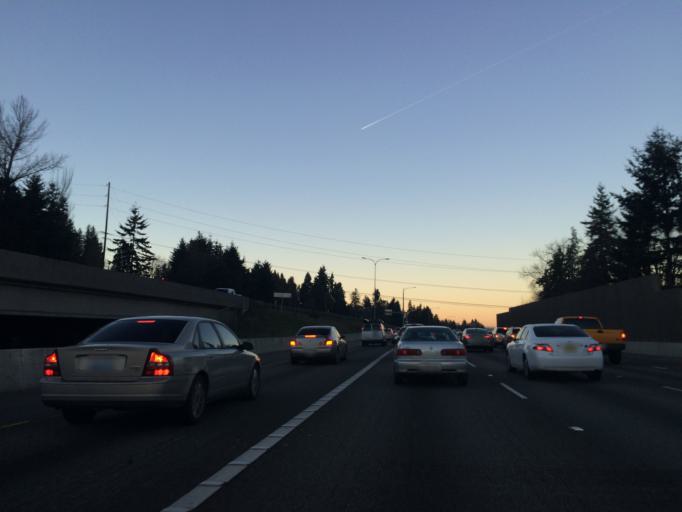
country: US
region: Washington
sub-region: Snohomish County
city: Everett
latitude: 47.9478
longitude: -122.1984
